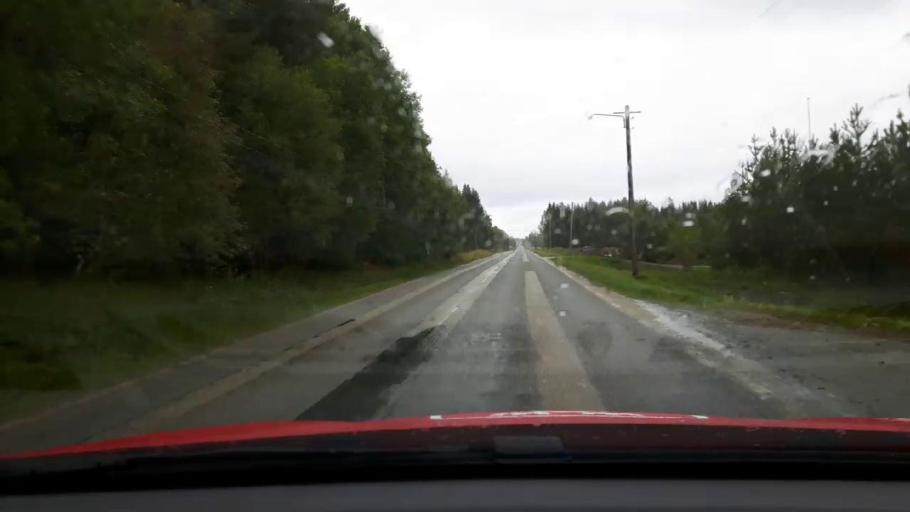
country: SE
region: Jaemtland
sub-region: Bergs Kommun
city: Hoverberg
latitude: 62.8240
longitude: 14.3925
